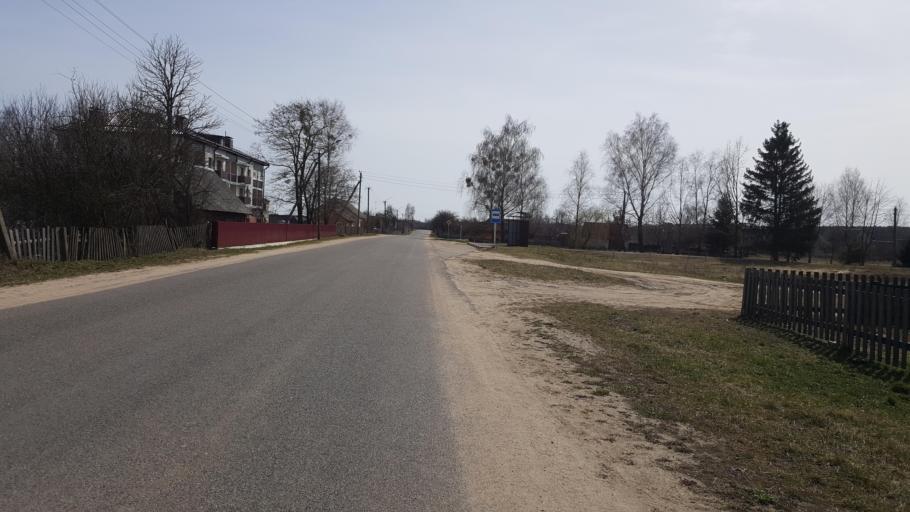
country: BY
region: Brest
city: Kamyanyuki
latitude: 52.4935
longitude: 23.8703
